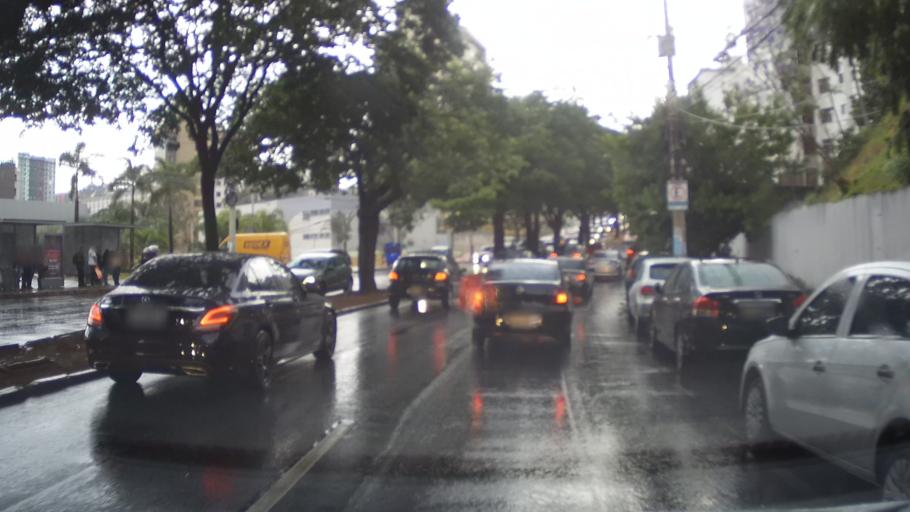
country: BR
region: Minas Gerais
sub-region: Belo Horizonte
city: Belo Horizonte
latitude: -19.9451
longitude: -43.9570
